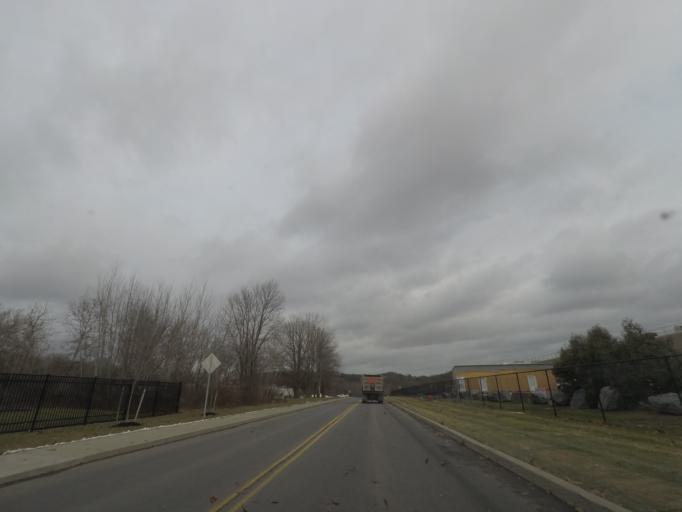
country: US
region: New York
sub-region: Rensselaer County
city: Hampton Manor
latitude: 42.6272
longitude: -73.7332
